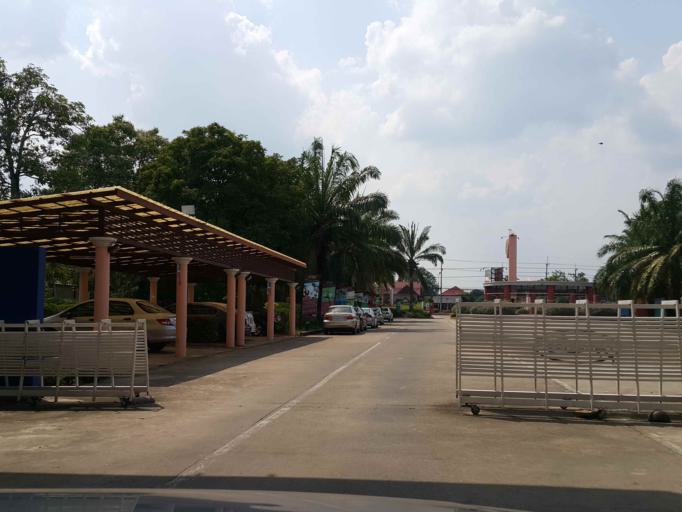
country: TH
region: Chiang Mai
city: Hang Dong
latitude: 18.7047
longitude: 98.9353
